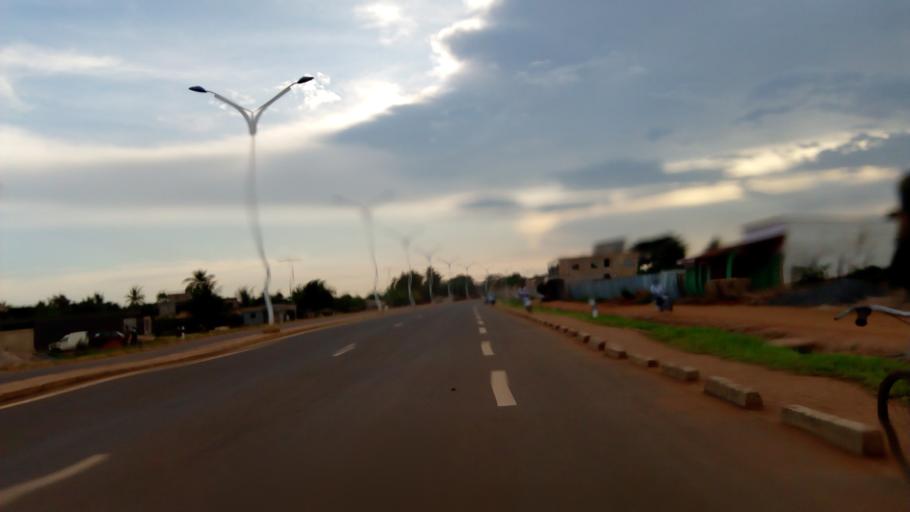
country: TG
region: Maritime
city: Lome
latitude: 6.2662
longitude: 1.1482
